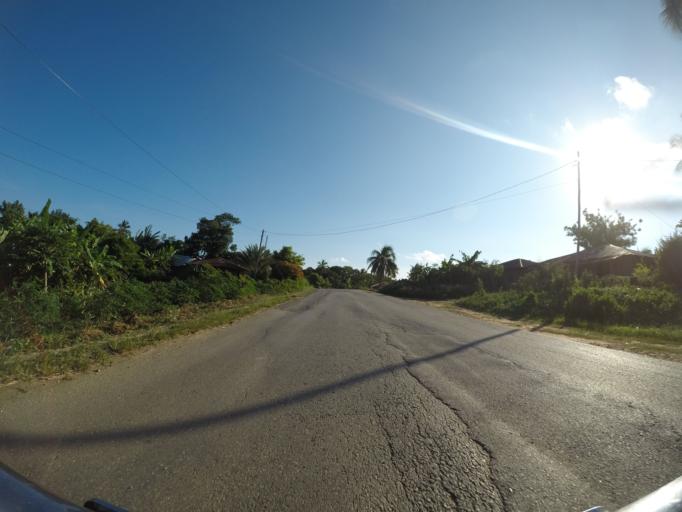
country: TZ
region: Pemba South
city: Chake Chake
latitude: -5.2831
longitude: 39.7652
